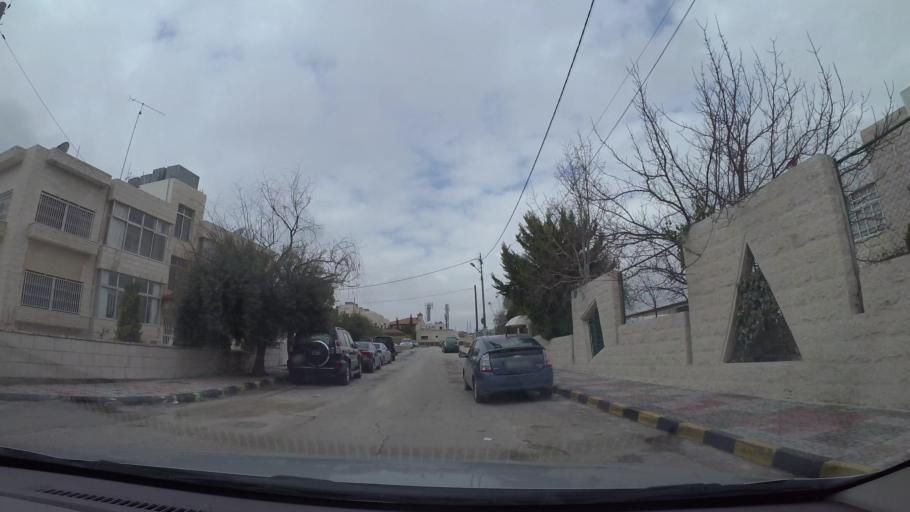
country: JO
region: Amman
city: Wadi as Sir
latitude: 31.9868
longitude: 35.8358
